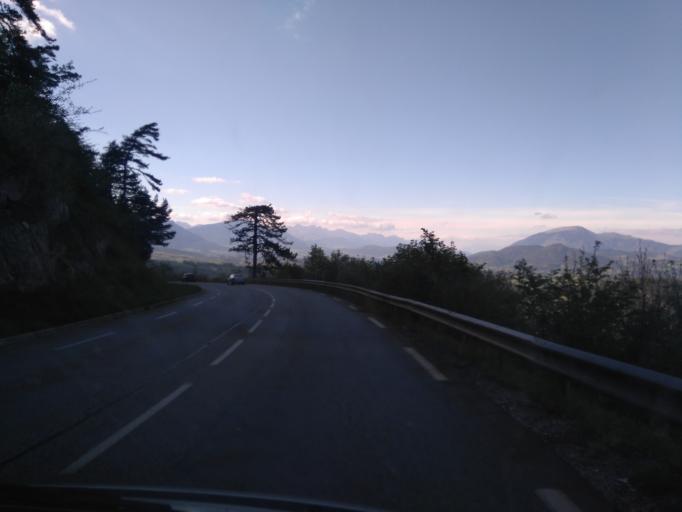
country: FR
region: Rhone-Alpes
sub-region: Departement de l'Isere
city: Mens
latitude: 44.7471
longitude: 5.6788
